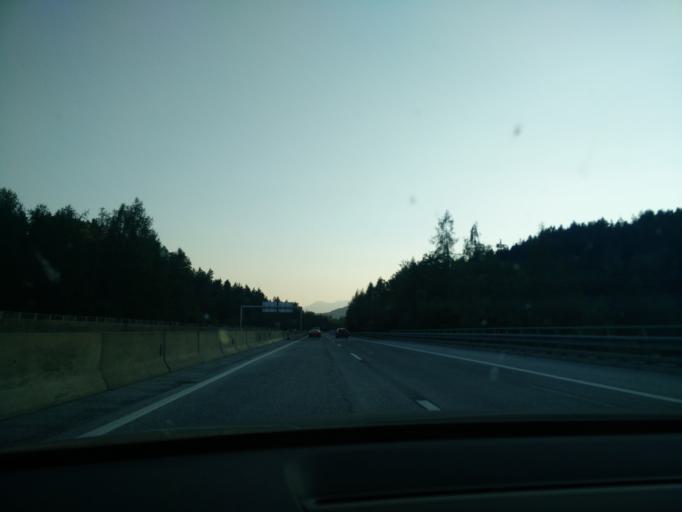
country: AT
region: Carinthia
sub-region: Politischer Bezirk Klagenfurt Land
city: Moosburg
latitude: 46.6299
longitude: 14.2013
